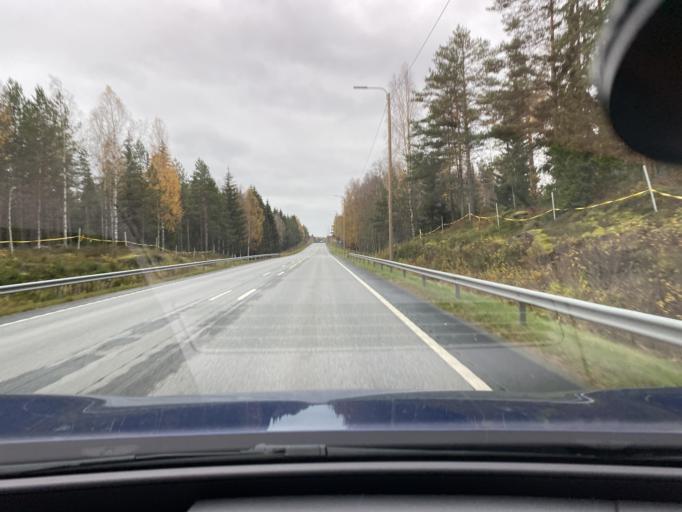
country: FI
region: Varsinais-Suomi
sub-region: Vakka-Suomi
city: Laitila
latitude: 60.9473
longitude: 21.5998
